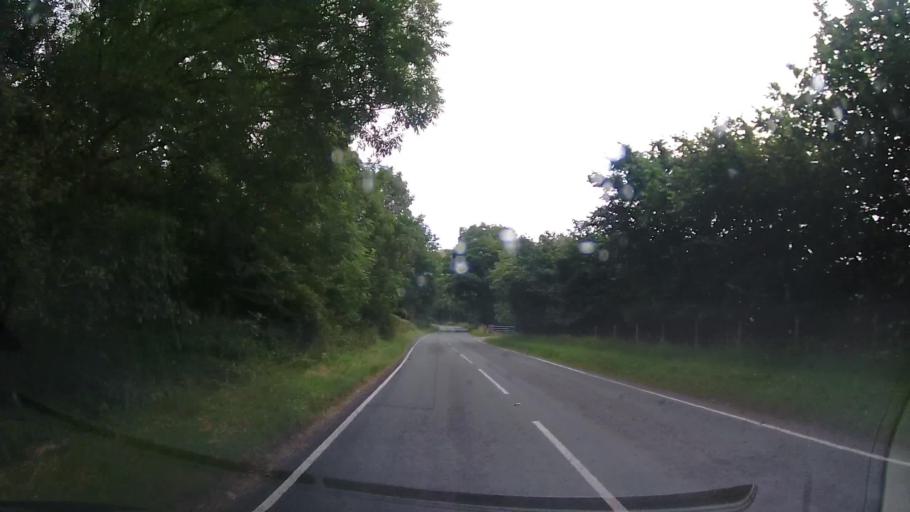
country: GB
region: Wales
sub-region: Sir Powys
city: Llangynog
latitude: 52.8456
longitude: -3.4263
